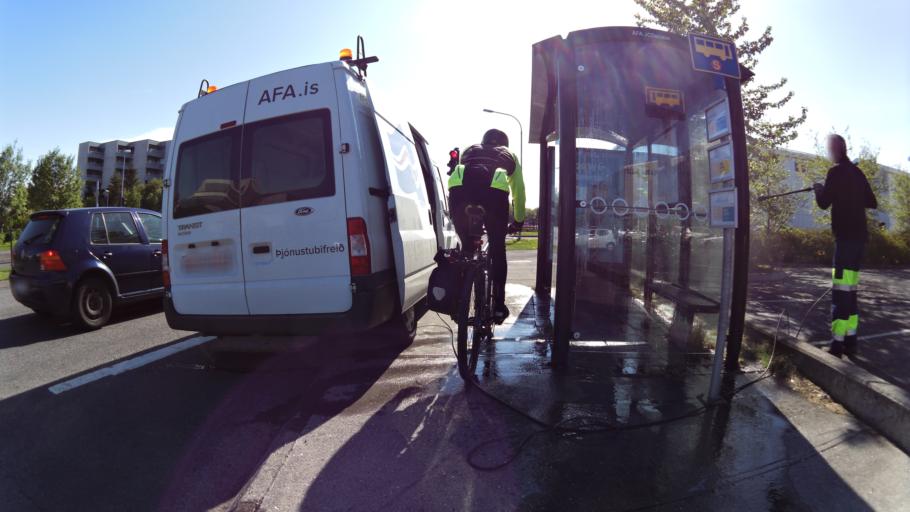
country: IS
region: Capital Region
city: Reykjavik
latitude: 64.1282
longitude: -21.8953
